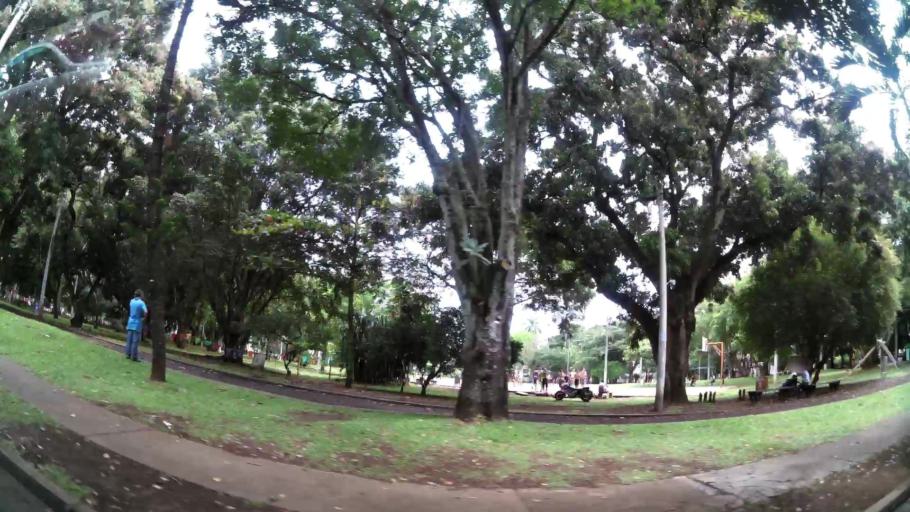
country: CO
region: Valle del Cauca
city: Cali
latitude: 3.3883
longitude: -76.5417
